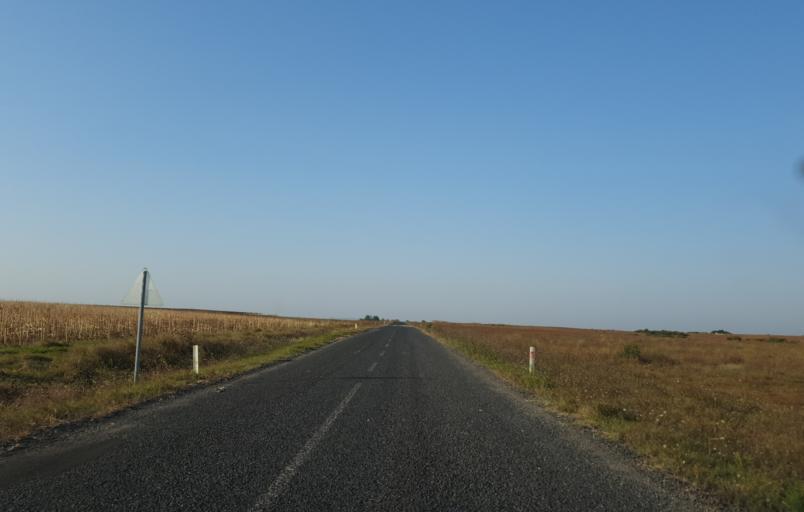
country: TR
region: Tekirdag
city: Beyazkoy
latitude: 41.4035
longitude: 27.7588
